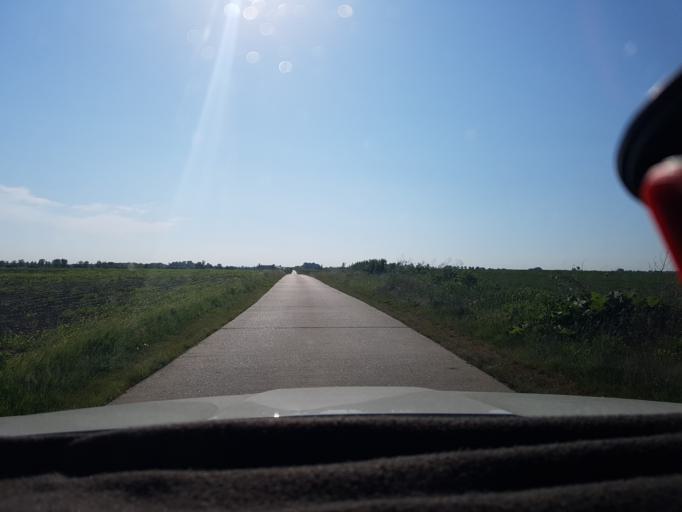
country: HU
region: Tolna
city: Decs
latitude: 46.2777
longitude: 18.7071
